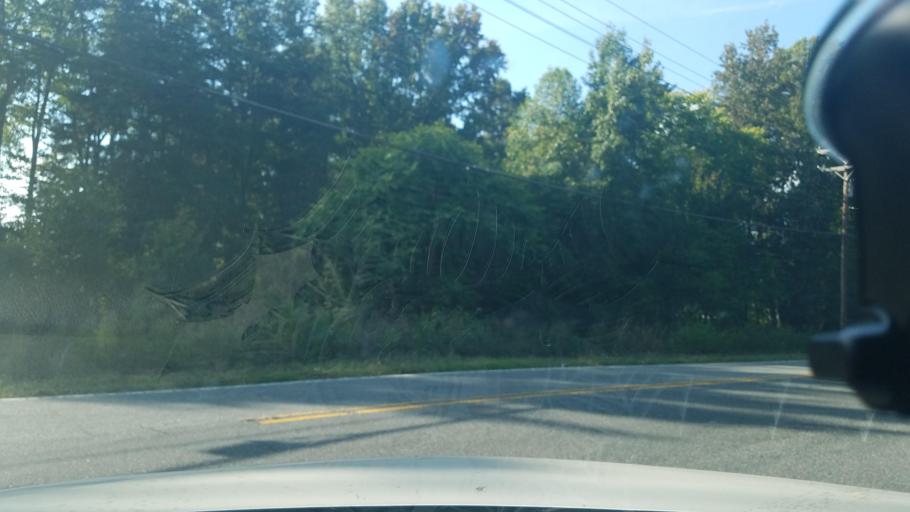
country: US
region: North Carolina
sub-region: Guilford County
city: Pleasant Garden
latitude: 36.0141
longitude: -79.7761
